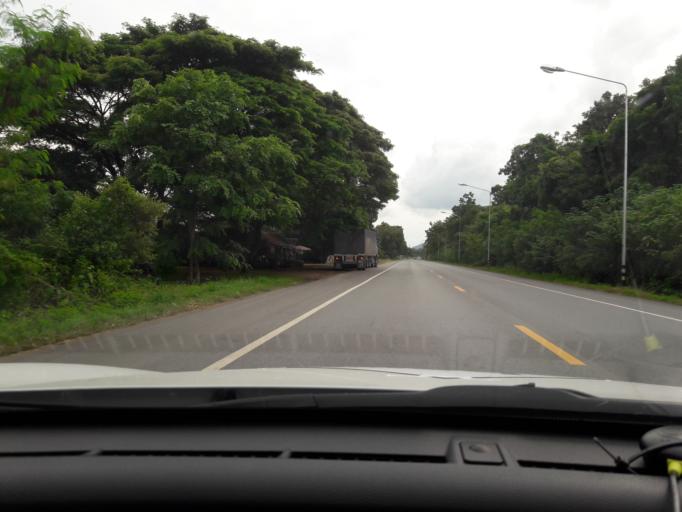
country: TH
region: Nakhon Sawan
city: Tak Fa
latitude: 15.3648
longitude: 100.5054
